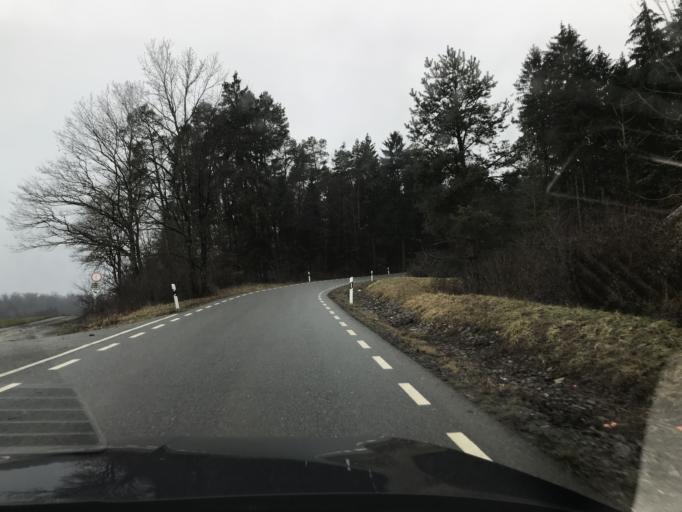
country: DE
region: Baden-Wuerttemberg
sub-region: Regierungsbezirk Stuttgart
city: Weil im Schonbuch
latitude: 48.6124
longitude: 9.0672
